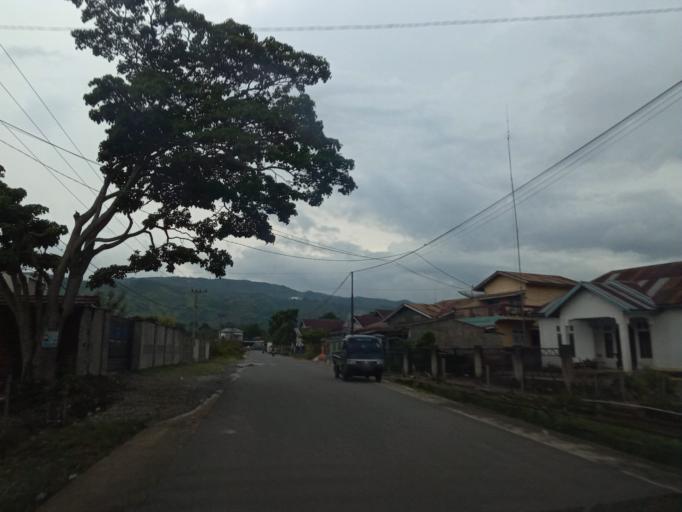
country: ID
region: Jambi
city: Semurup
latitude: -1.9886
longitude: 101.3613
